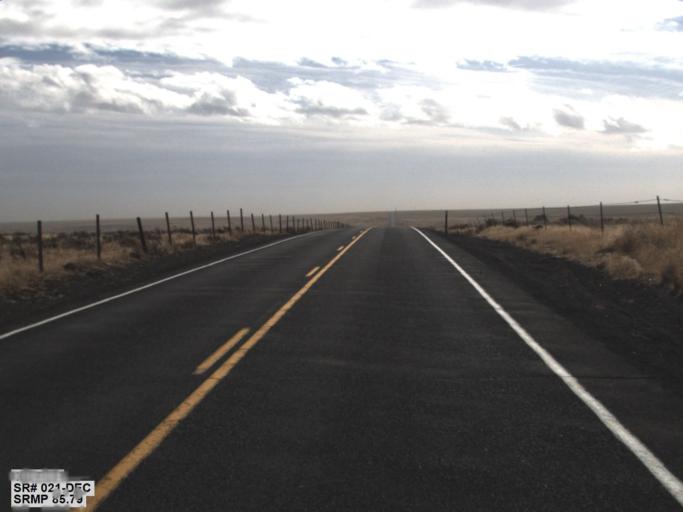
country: US
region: Washington
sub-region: Okanogan County
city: Coulee Dam
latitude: 47.6806
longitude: -118.7218
